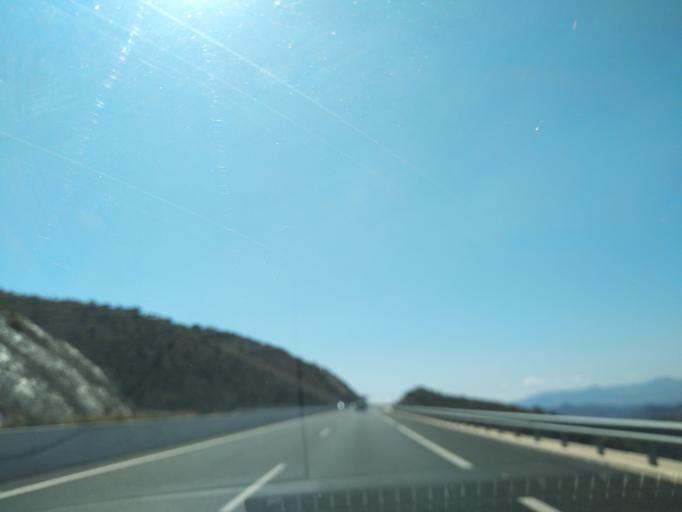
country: ES
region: Andalusia
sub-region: Provincia de Malaga
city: Almogia
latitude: 36.8502
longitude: -4.4842
